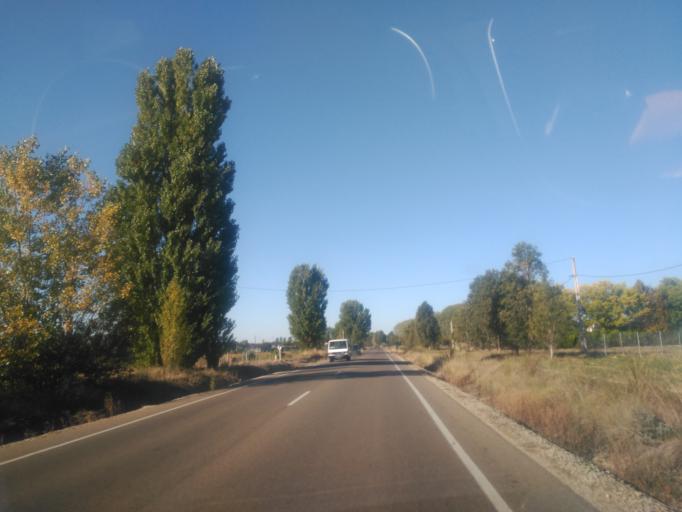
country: ES
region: Castille and Leon
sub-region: Provincia de Burgos
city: Fresnillo de las Duenas
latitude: 41.6806
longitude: -3.6376
